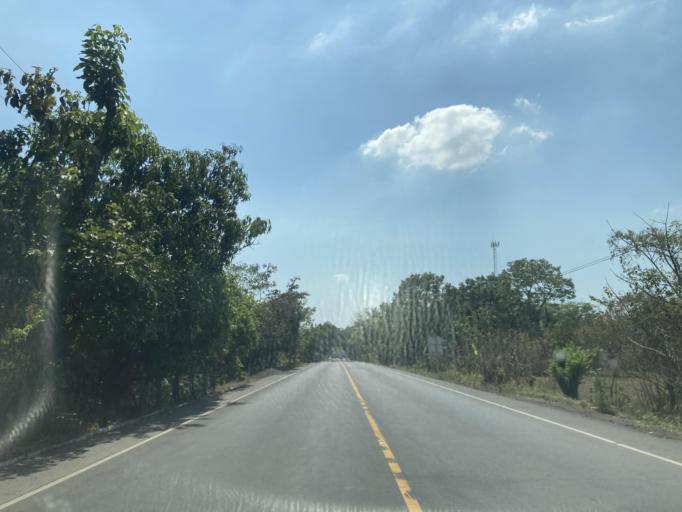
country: GT
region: Escuintla
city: Guanagazapa
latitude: 14.2045
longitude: -90.7146
